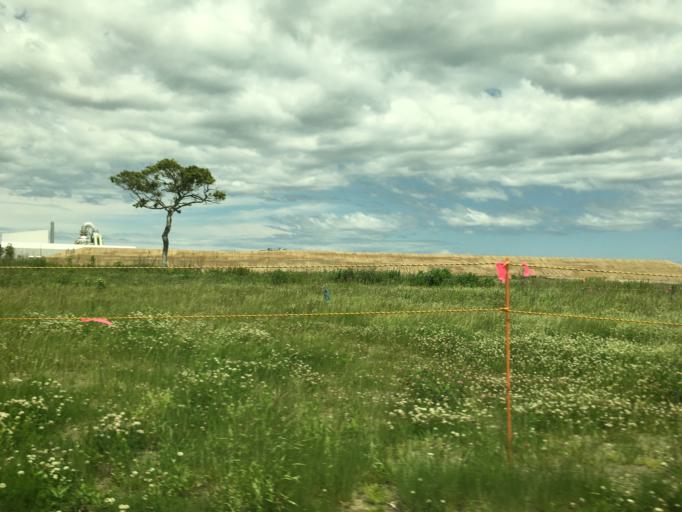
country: JP
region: Fukushima
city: Namie
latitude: 37.4842
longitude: 141.0347
